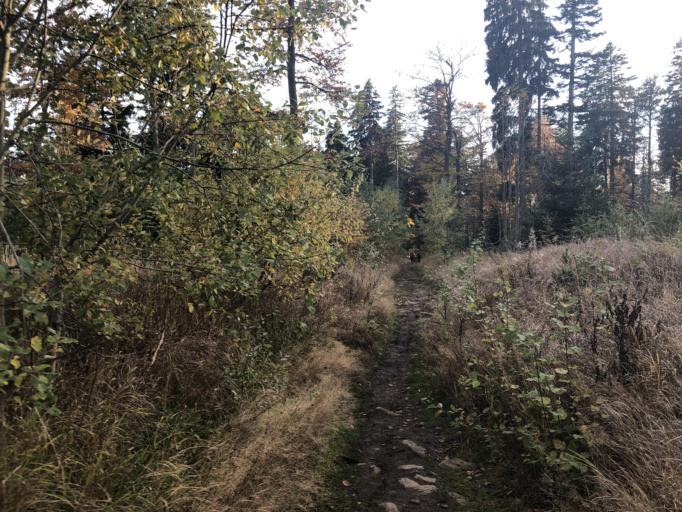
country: DE
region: Bavaria
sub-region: Lower Bavaria
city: Bodenmais
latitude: 49.0761
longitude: 13.1571
